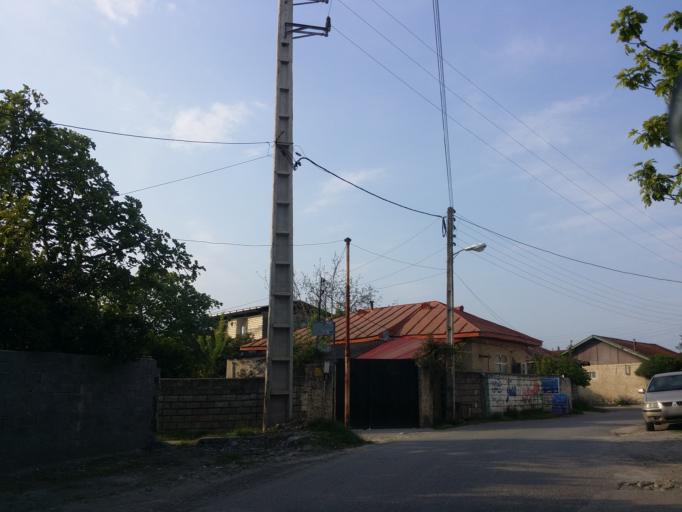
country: IR
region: Mazandaran
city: Chalus
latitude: 36.6645
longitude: 51.3746
